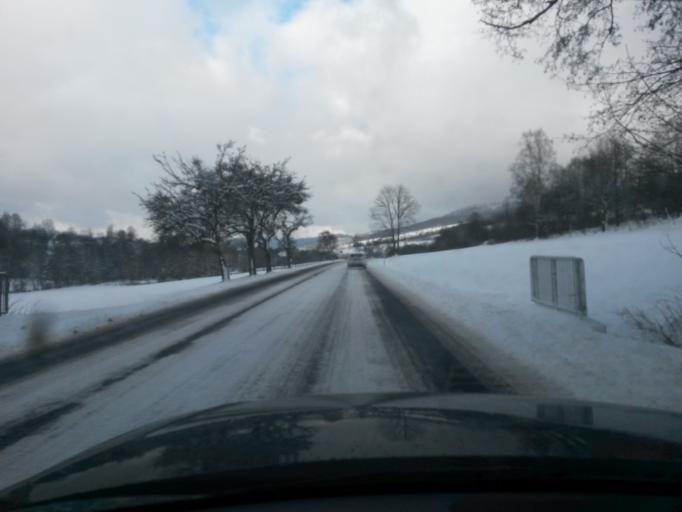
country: DE
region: Thuringia
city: Birx
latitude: 50.5146
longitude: 10.0170
